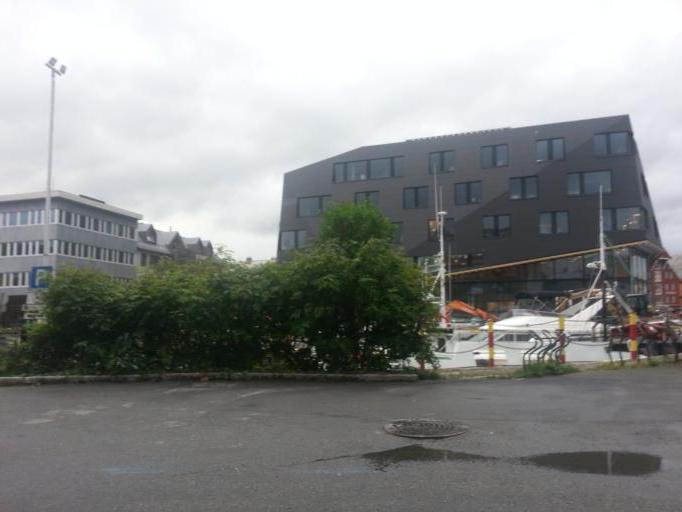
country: NO
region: Troms
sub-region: Tromso
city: Tromso
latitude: 69.6510
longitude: 18.9598
